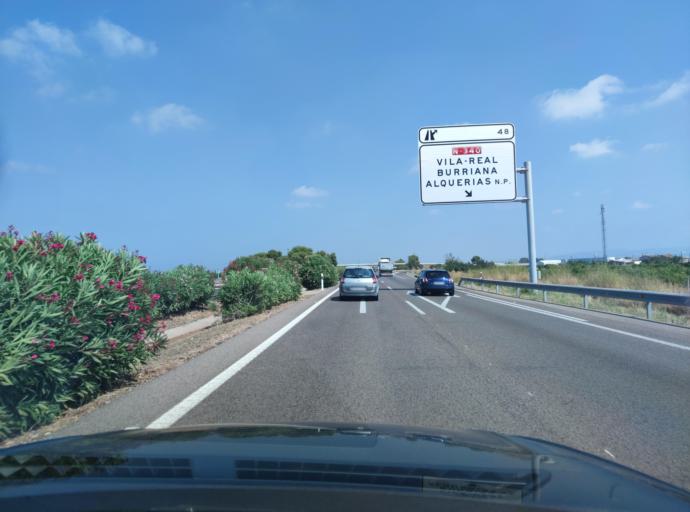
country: ES
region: Valencia
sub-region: Provincia de Castello
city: Alquerias del Nino Perdido
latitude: 39.8932
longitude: -0.1295
